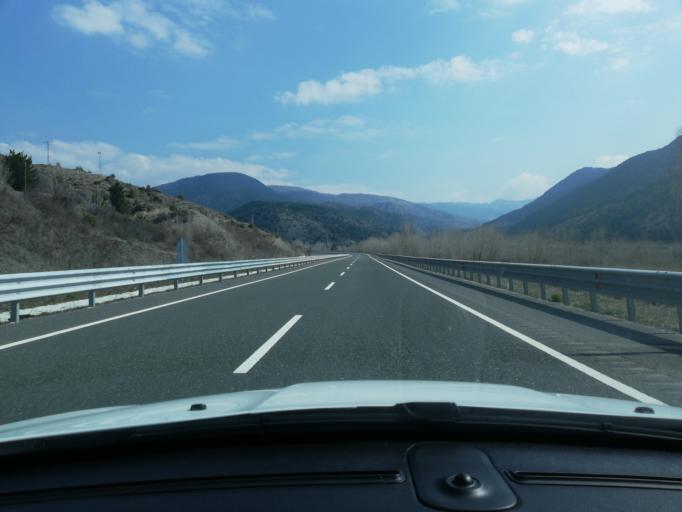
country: TR
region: Cankiri
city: Ilgaz
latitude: 40.9718
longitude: 33.6917
